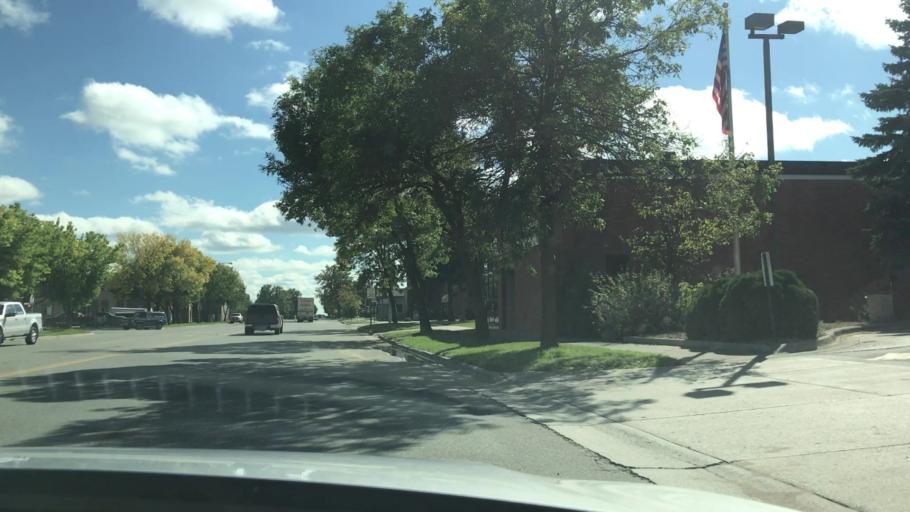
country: US
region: Minnesota
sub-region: Hubbard County
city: Park Rapids
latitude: 46.9218
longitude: -95.0585
